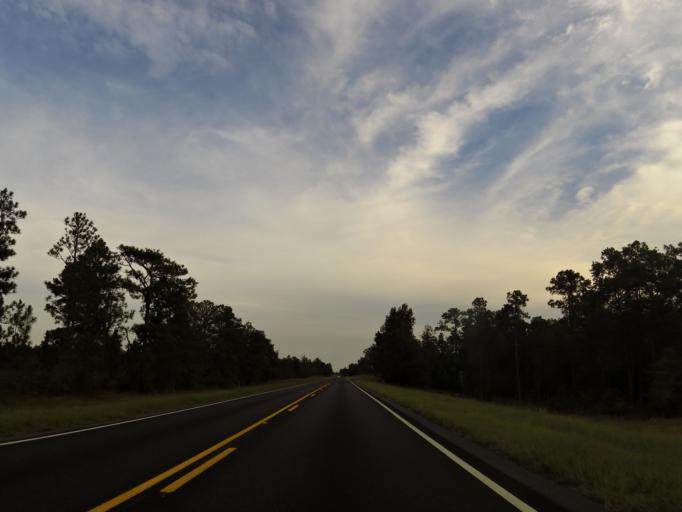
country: US
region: Alabama
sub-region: Monroe County
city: Frisco City
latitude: 31.2447
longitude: -87.4887
